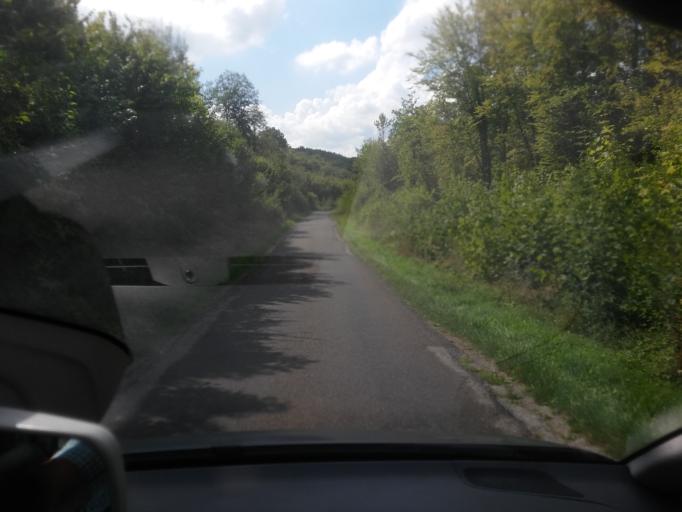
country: FR
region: Lorraine
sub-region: Departement de la Meuse
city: Montmedy
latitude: 49.4958
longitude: 5.4168
